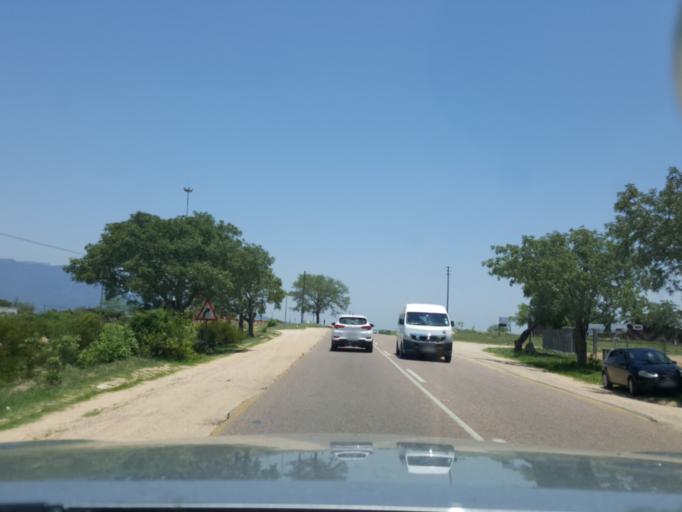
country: ZA
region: Limpopo
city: Thulamahashi
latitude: -24.5923
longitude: 31.0423
